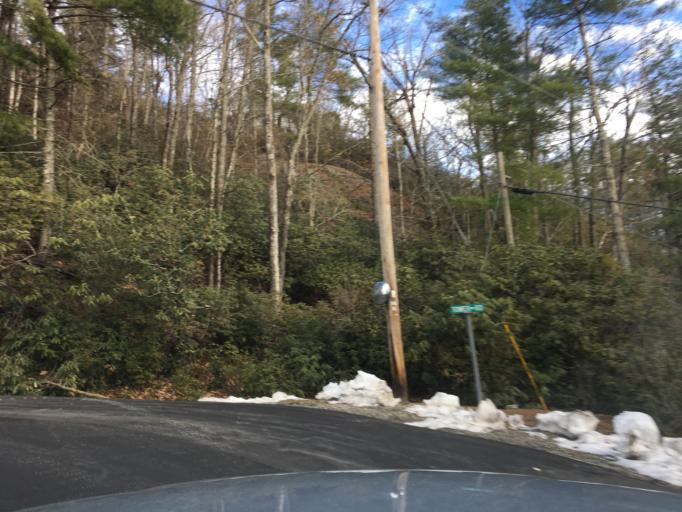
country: US
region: North Carolina
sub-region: Jackson County
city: Cullowhee
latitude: 35.1281
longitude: -83.0095
